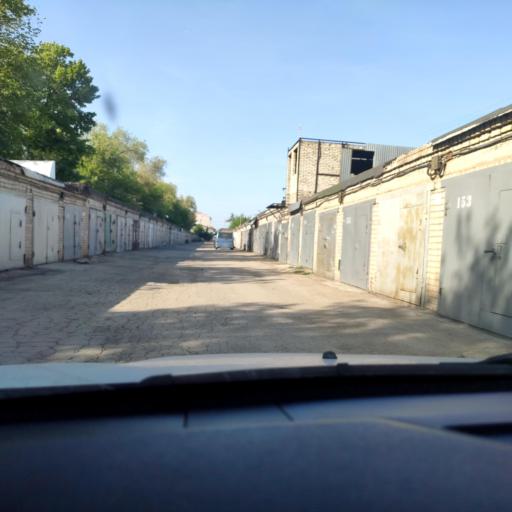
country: RU
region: Samara
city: Smyshlyayevka
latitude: 53.2196
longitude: 50.2796
